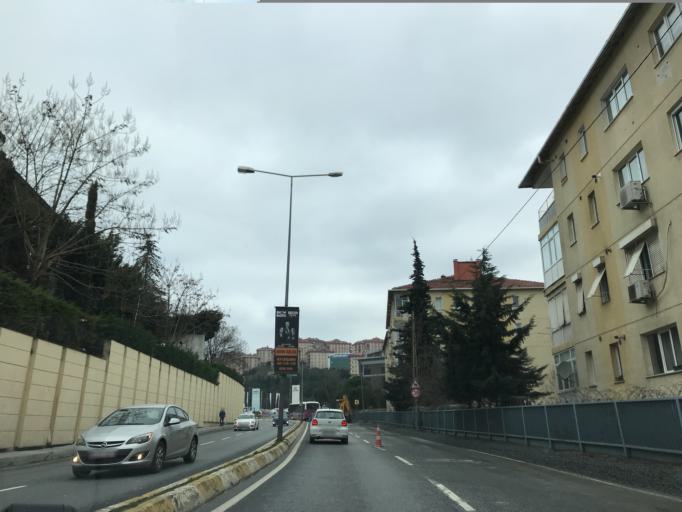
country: TR
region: Istanbul
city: Sisli
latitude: 41.1219
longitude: 29.0435
